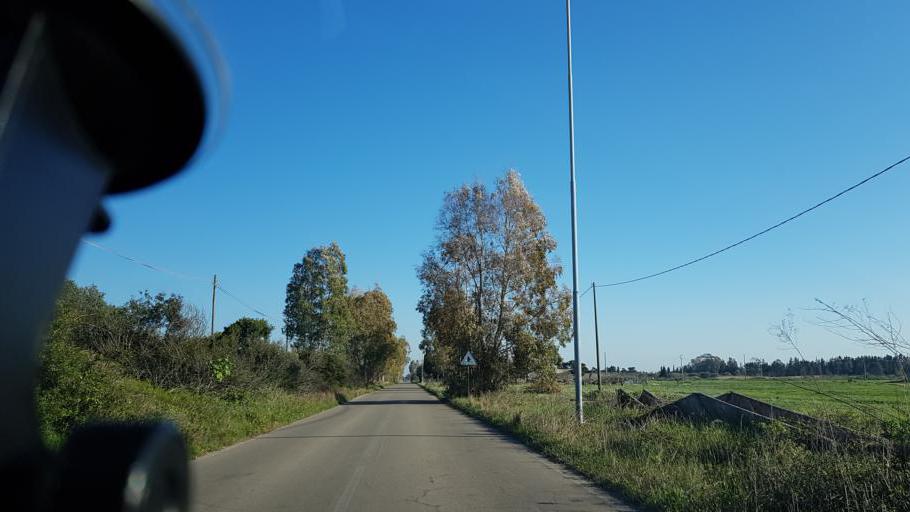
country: IT
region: Apulia
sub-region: Provincia di Lecce
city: Merine
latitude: 40.4231
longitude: 18.2467
